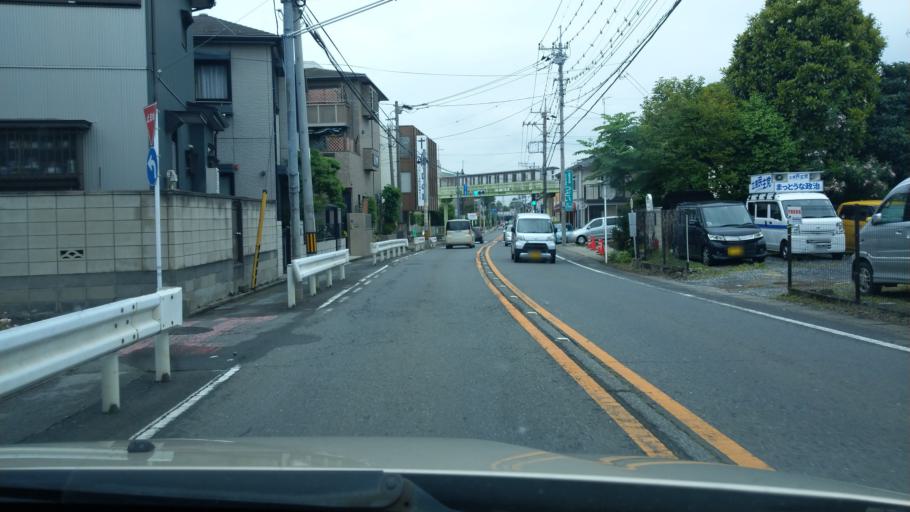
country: JP
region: Saitama
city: Saitama
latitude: 35.9130
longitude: 139.6340
